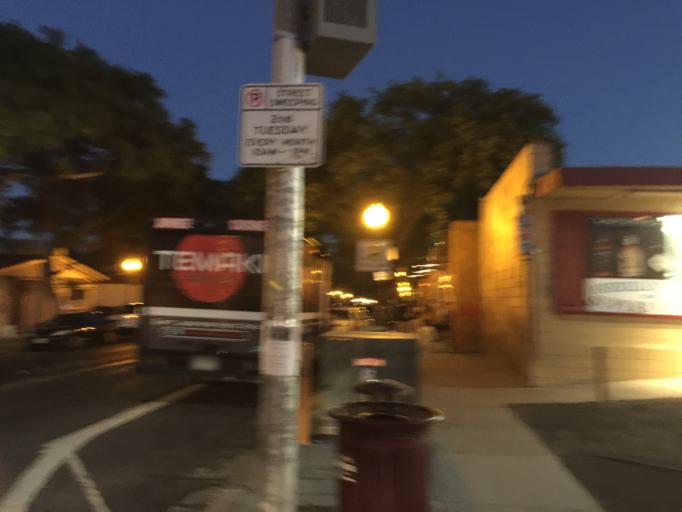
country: US
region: California
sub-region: San Diego County
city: San Diego
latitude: 32.7296
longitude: -117.1297
